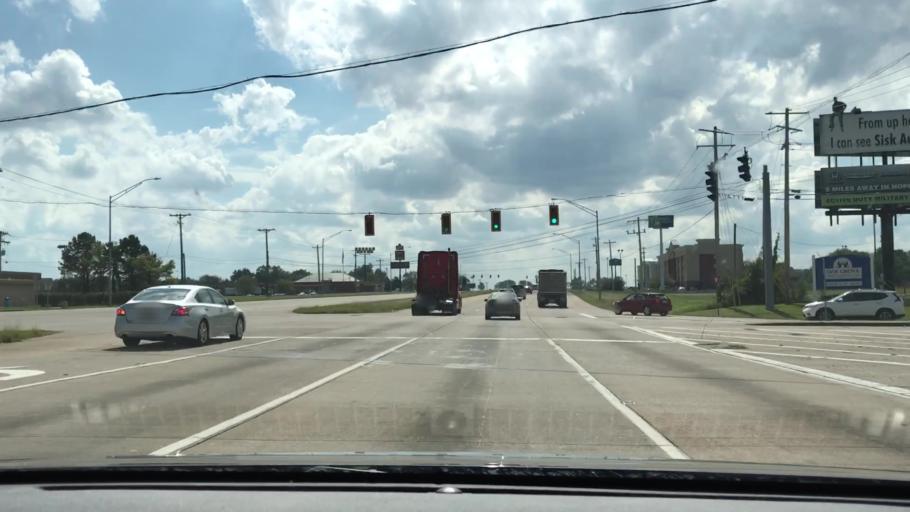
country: US
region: Kentucky
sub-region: Christian County
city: Oak Grove
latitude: 36.6965
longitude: -87.4534
